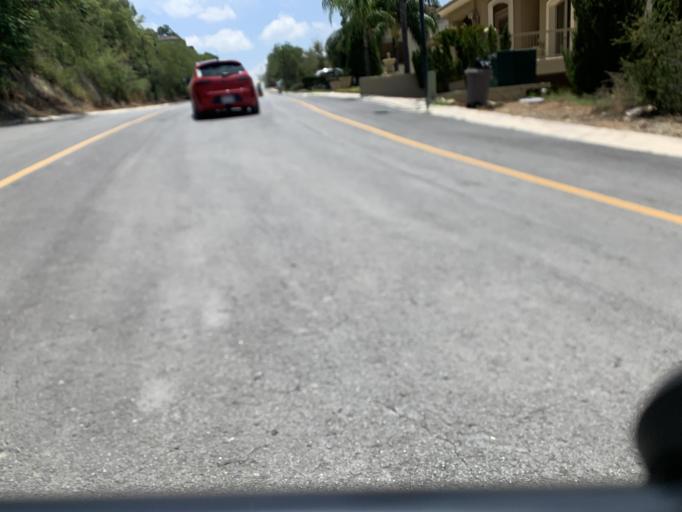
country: MX
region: Nuevo Leon
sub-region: Juarez
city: Bosques de San Pedro
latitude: 25.5194
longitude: -100.1875
